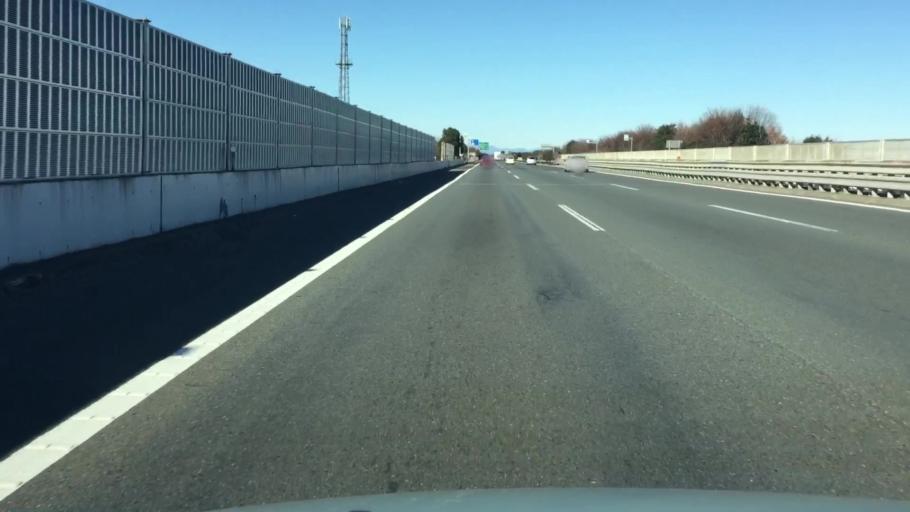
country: JP
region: Saitama
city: Yorii
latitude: 36.1287
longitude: 139.2407
